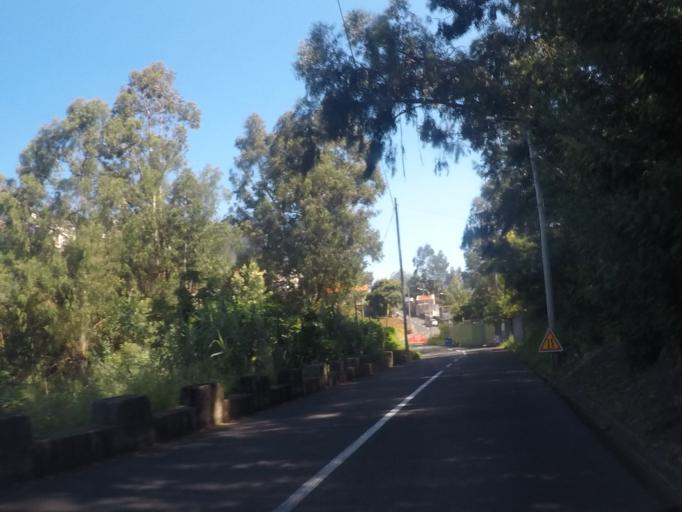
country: PT
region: Madeira
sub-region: Camara de Lobos
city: Curral das Freiras
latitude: 32.6796
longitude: -16.9672
